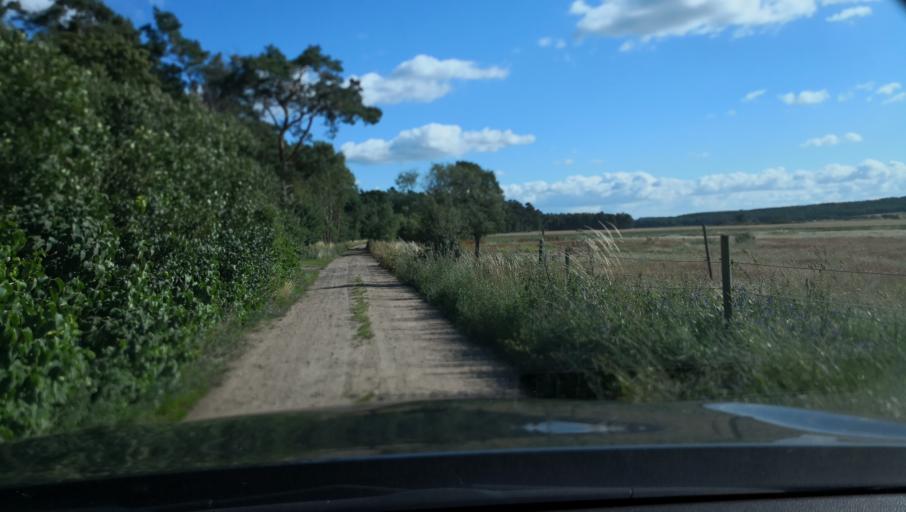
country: SE
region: Skane
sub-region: Kristianstads Kommun
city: Degeberga
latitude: 55.8056
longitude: 14.1967
